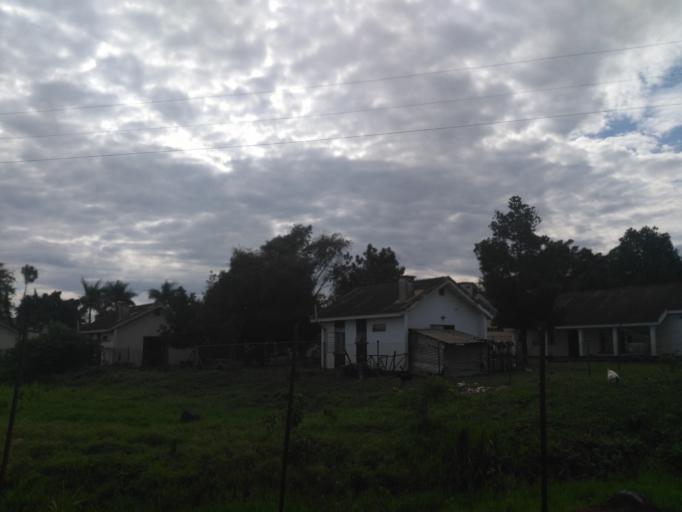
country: UG
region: Eastern Region
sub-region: Jinja District
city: Jinja
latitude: 0.4421
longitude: 33.1937
